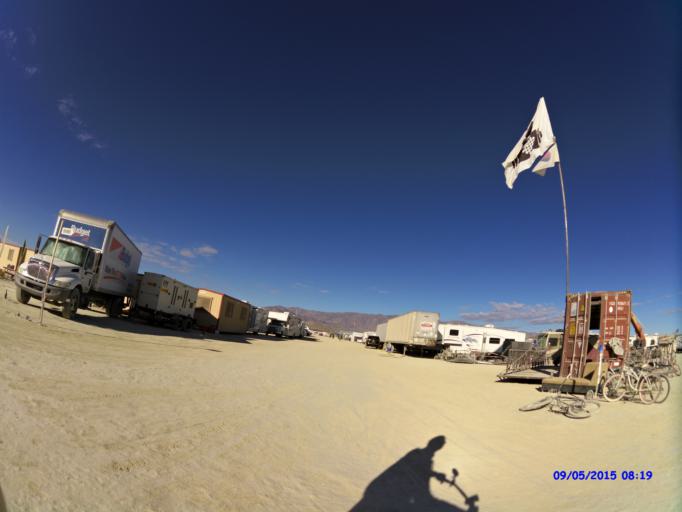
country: US
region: Nevada
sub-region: Pershing County
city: Lovelock
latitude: 40.8000
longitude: -119.2114
